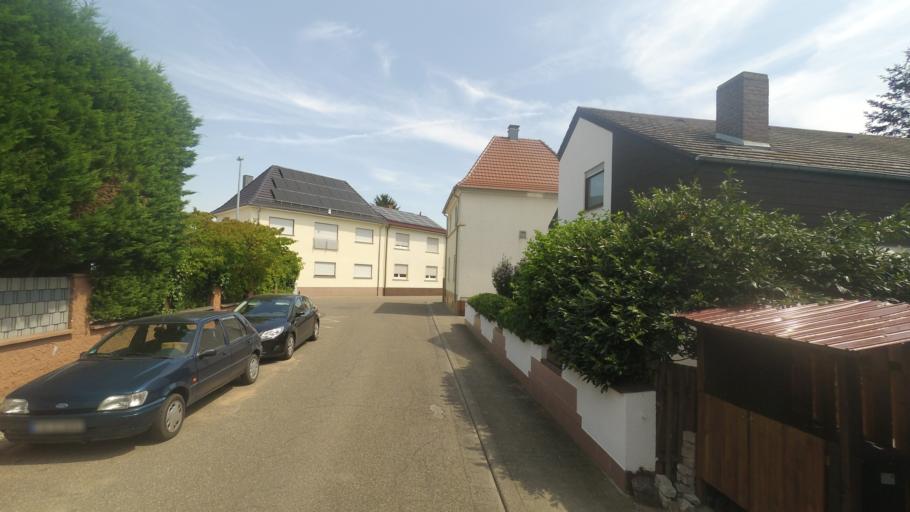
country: DE
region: Rheinland-Pfalz
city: Schifferstadt
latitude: 49.3843
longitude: 8.3835
